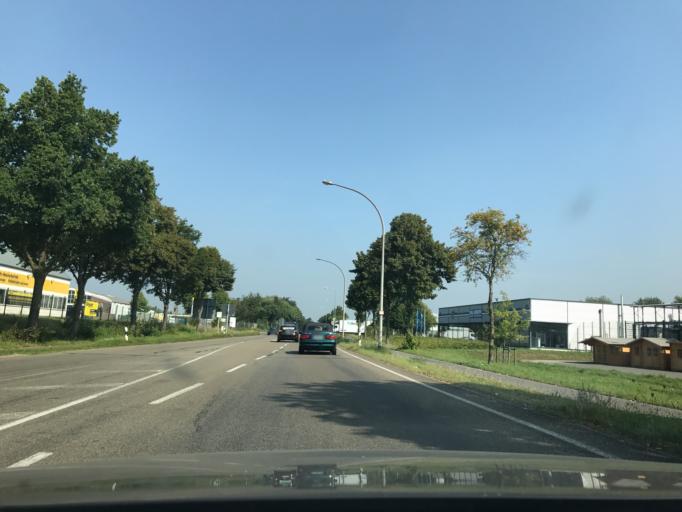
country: DE
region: North Rhine-Westphalia
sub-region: Regierungsbezirk Dusseldorf
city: Kleve
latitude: 51.8011
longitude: 6.1383
